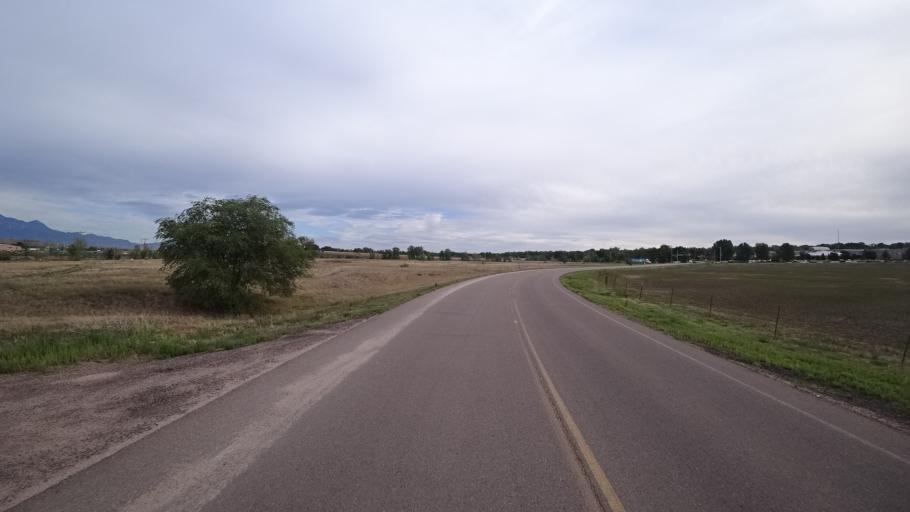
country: US
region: Colorado
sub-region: El Paso County
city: Security-Widefield
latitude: 38.7188
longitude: -104.7140
